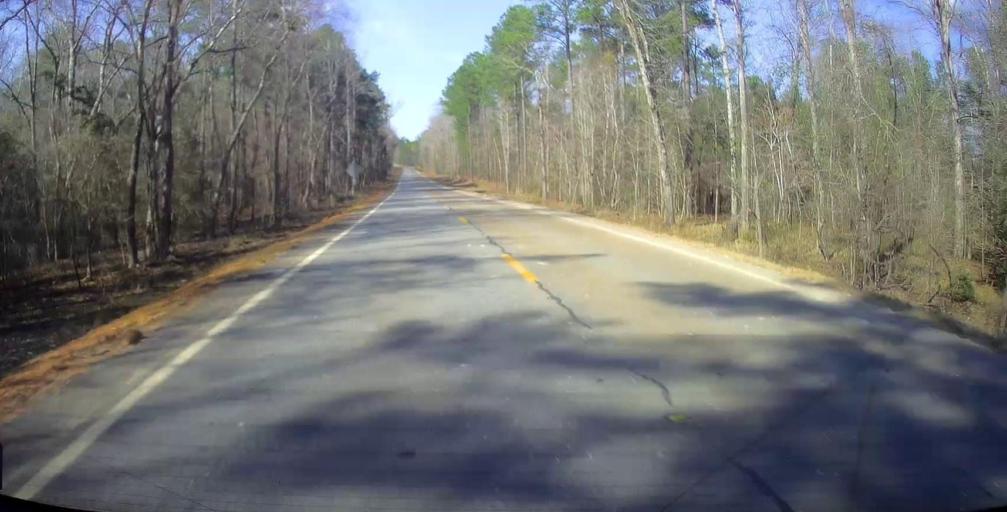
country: US
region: Georgia
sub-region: Wilkinson County
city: Gordon
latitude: 32.8164
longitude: -83.3244
